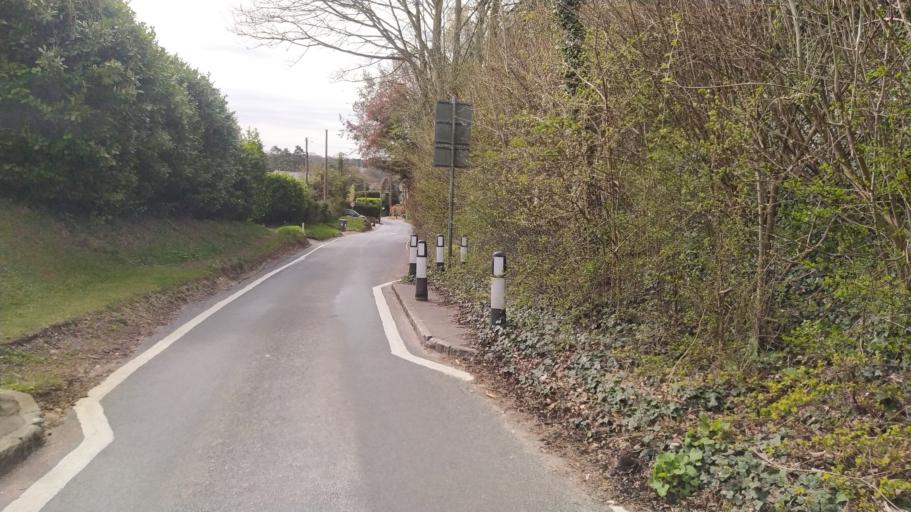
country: GB
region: England
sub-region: Hampshire
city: Bishops Waltham
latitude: 50.9679
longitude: -1.2089
